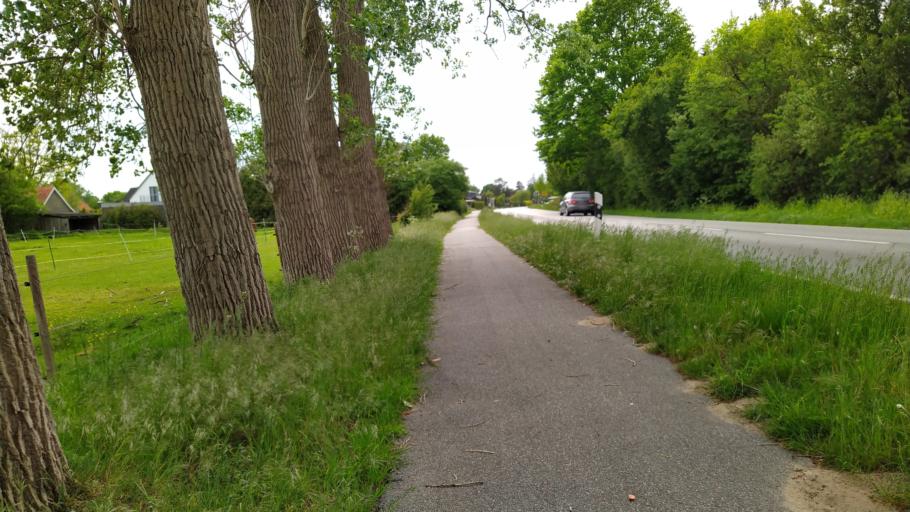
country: DE
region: Lower Saxony
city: Tarmstedt
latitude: 53.2272
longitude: 9.0932
